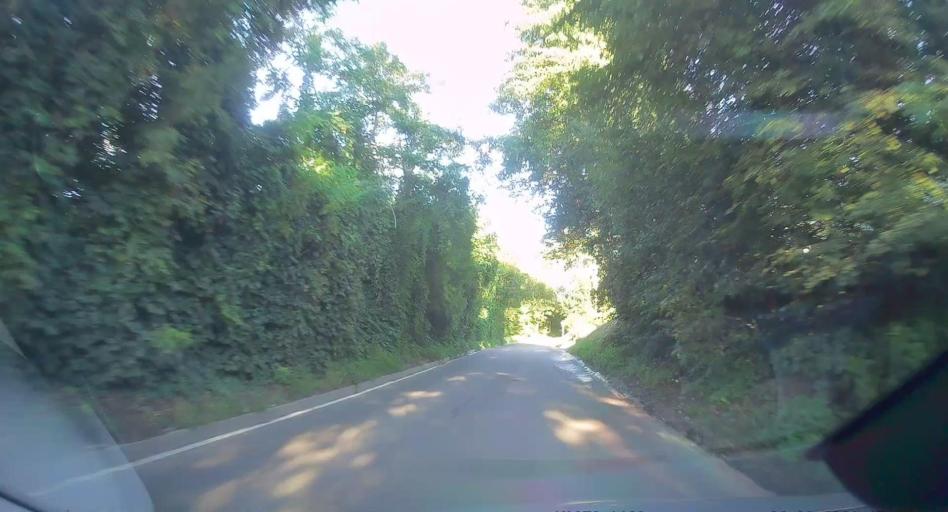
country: PL
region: Lesser Poland Voivodeship
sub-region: Powiat wielicki
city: Czarnochowice
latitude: 50.0156
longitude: 20.0550
